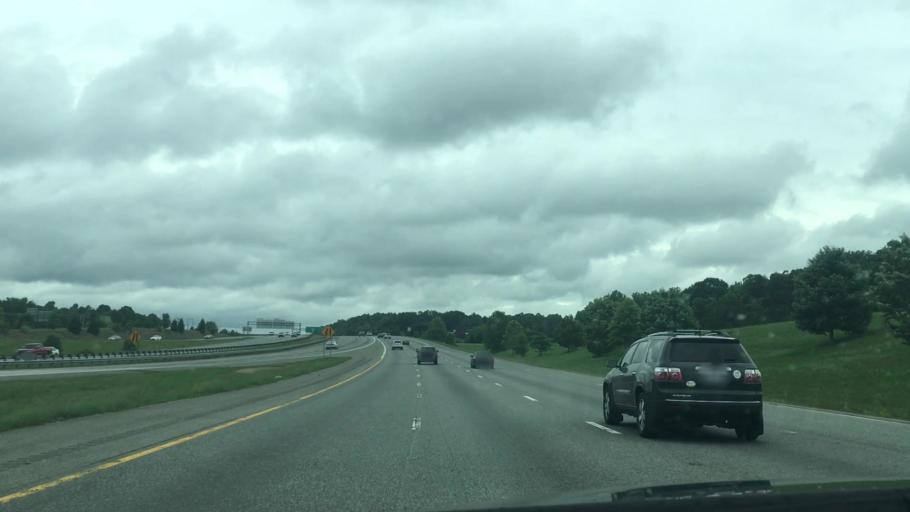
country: US
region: North Carolina
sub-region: Guilford County
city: Jamestown
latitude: 36.0025
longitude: -79.8576
